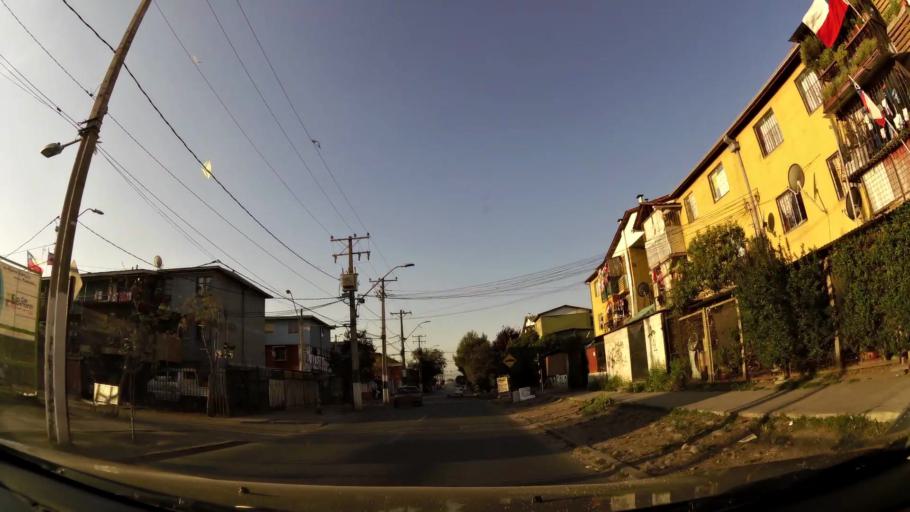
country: CL
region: Santiago Metropolitan
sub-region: Provincia de Maipo
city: San Bernardo
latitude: -33.5980
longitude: -70.6742
